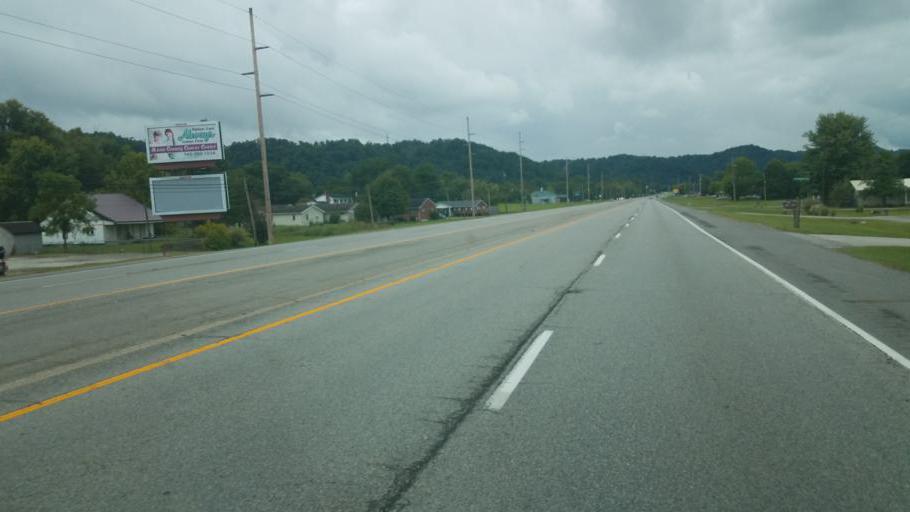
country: US
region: Kentucky
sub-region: Greenup County
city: South Shore
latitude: 38.7259
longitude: -82.9421
